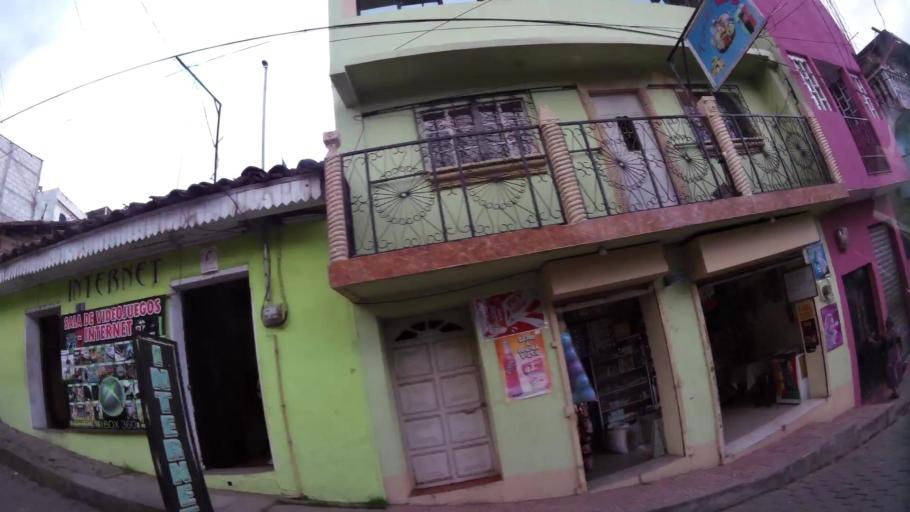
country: GT
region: Quiche
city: Chichicastenango
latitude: 14.9435
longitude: -91.1132
